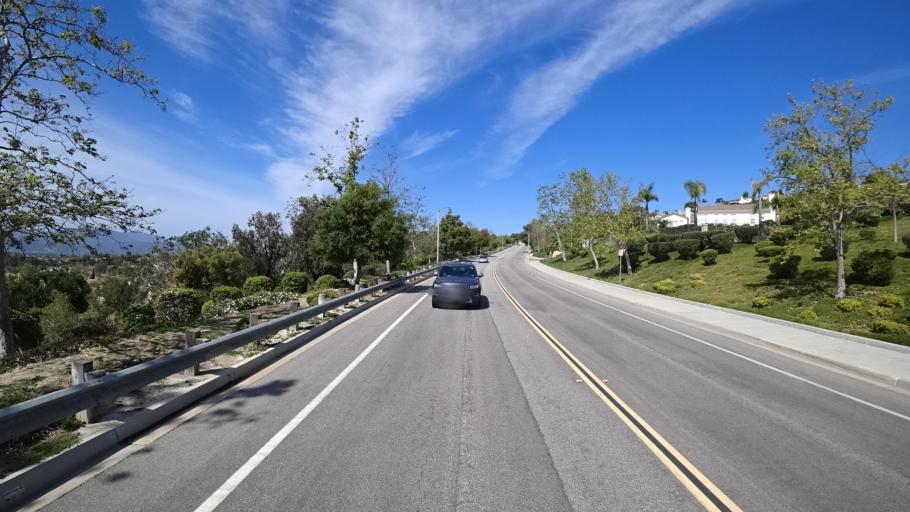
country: US
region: California
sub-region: Ventura County
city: Thousand Oaks
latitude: 34.2229
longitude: -118.8319
